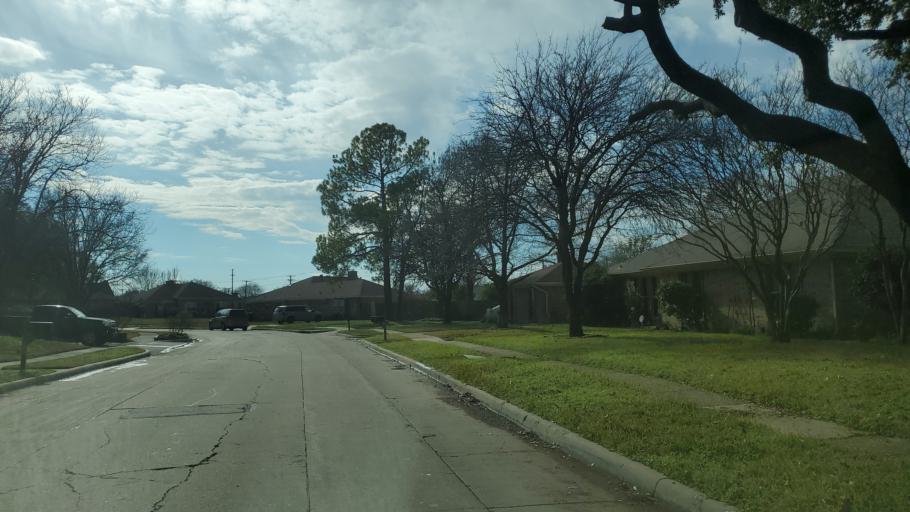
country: US
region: Texas
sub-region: Dallas County
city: Carrollton
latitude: 32.9804
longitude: -96.8830
